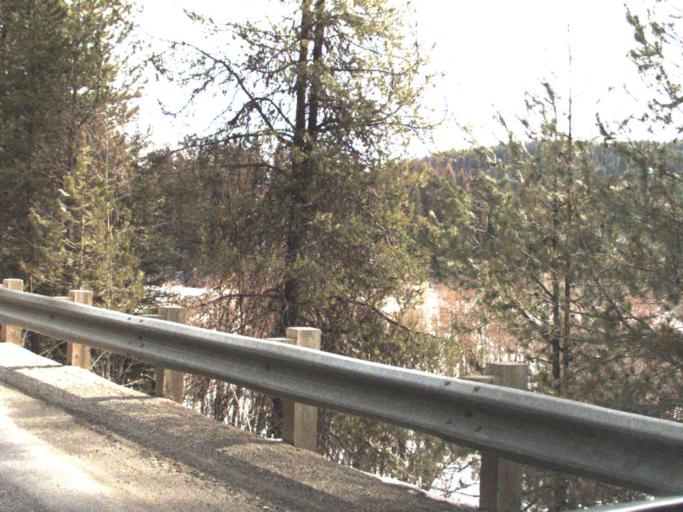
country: US
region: Washington
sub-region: Stevens County
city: Colville
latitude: 48.6418
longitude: -117.5185
